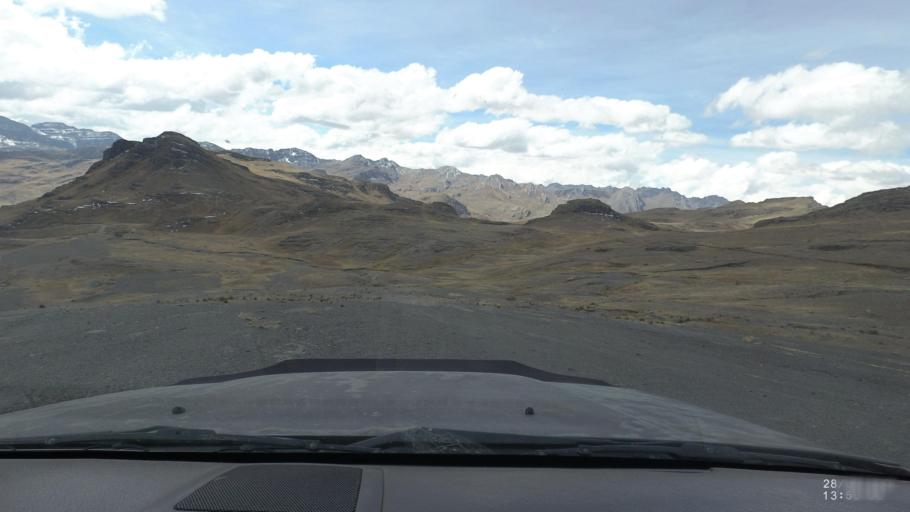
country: BO
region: Cochabamba
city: Sipe Sipe
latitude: -17.2781
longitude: -66.3810
